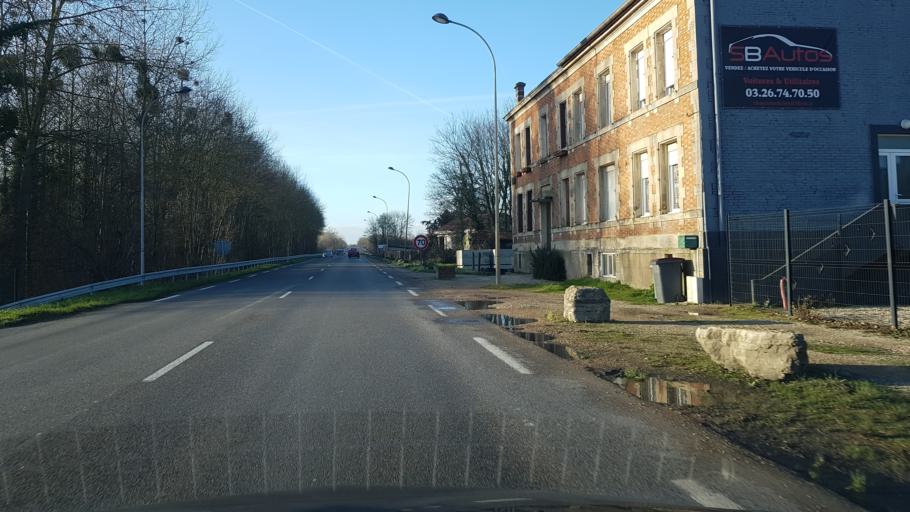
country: FR
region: Champagne-Ardenne
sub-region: Departement de la Marne
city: Vitry-le-Francois
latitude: 48.7295
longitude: 4.5734
